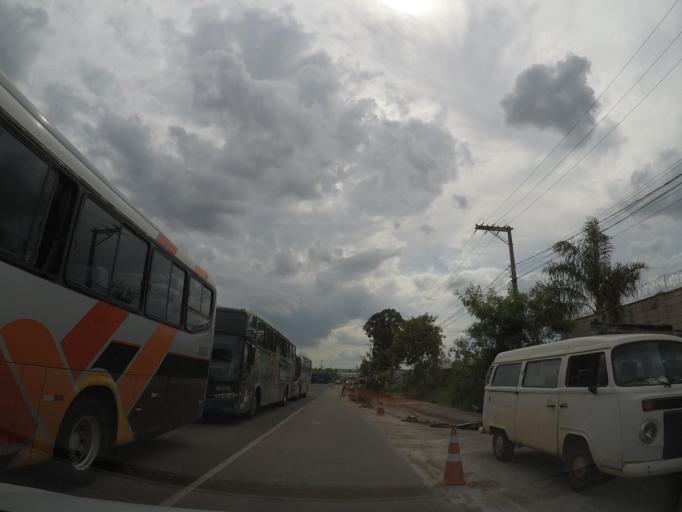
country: BR
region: Sao Paulo
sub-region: Sumare
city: Sumare
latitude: -22.8028
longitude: -47.2380
